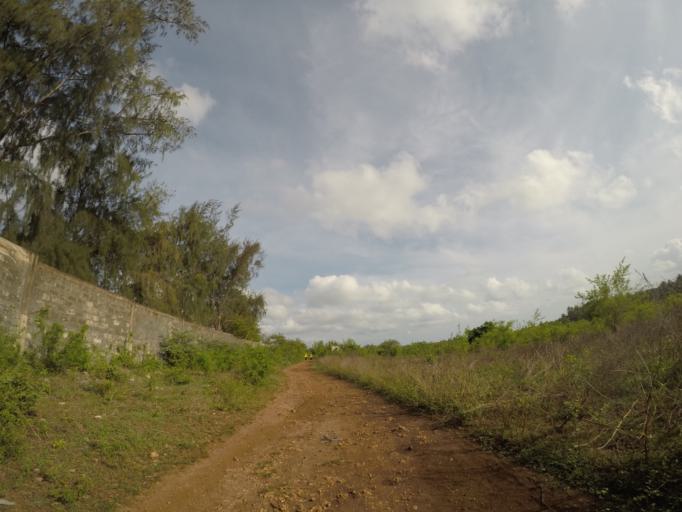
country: TZ
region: Zanzibar Central/South
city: Koani
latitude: -6.2263
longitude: 39.3098
